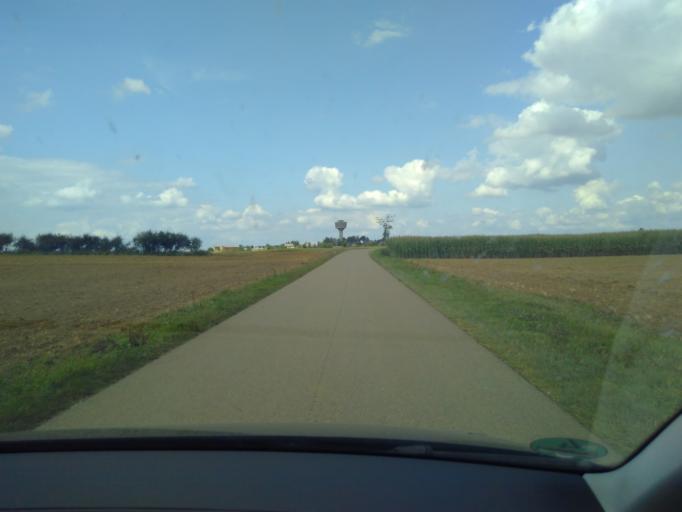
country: DE
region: Baden-Wuerttemberg
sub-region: Tuebingen Region
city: Berghulen
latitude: 48.4837
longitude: 9.7344
